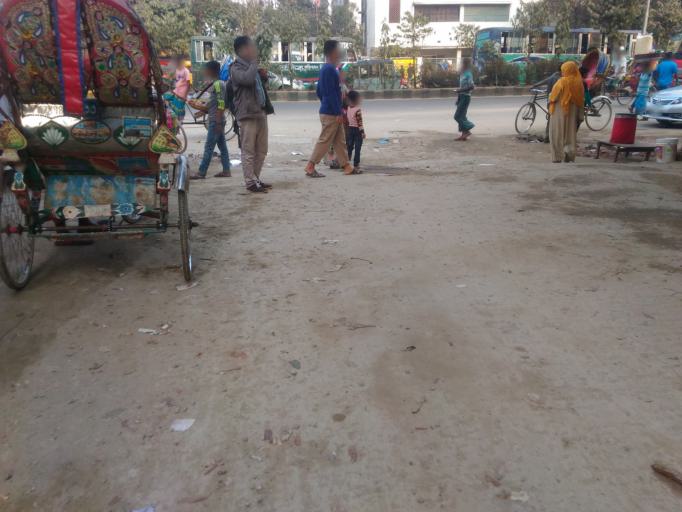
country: BD
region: Dhaka
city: Azimpur
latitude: 23.7914
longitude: 90.3538
